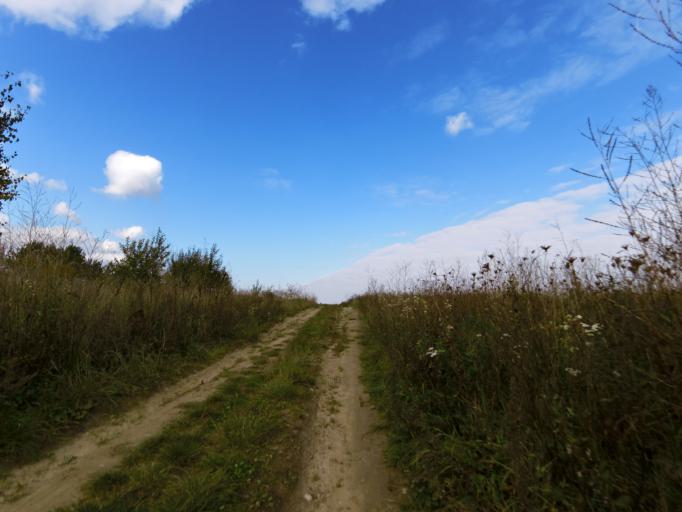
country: LT
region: Vilnius County
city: Pilaite
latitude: 54.7030
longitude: 25.1538
